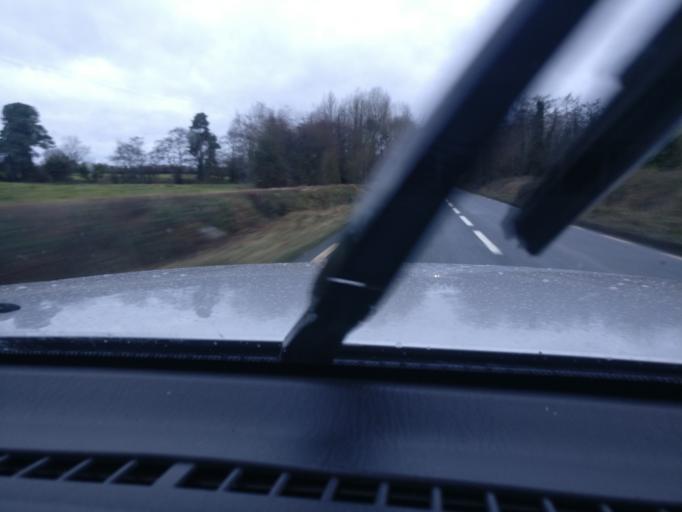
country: IE
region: Leinster
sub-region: An Mhi
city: Trim
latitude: 53.5232
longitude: -6.8215
